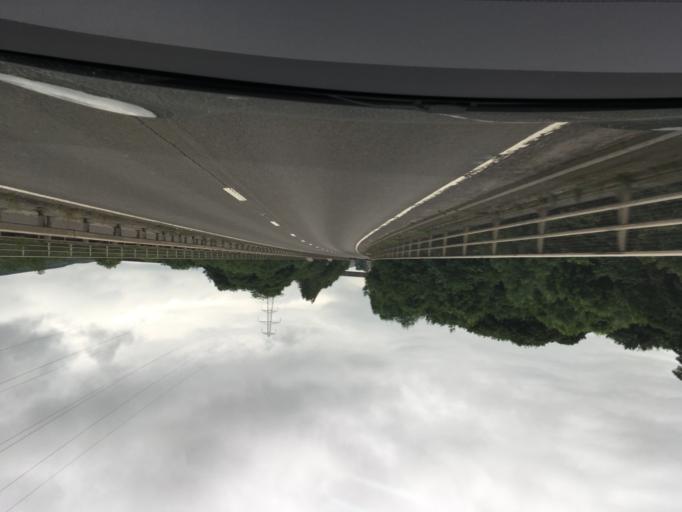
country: GB
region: England
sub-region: Derbyshire
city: Chapel en le Frith
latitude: 53.3315
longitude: -1.9117
